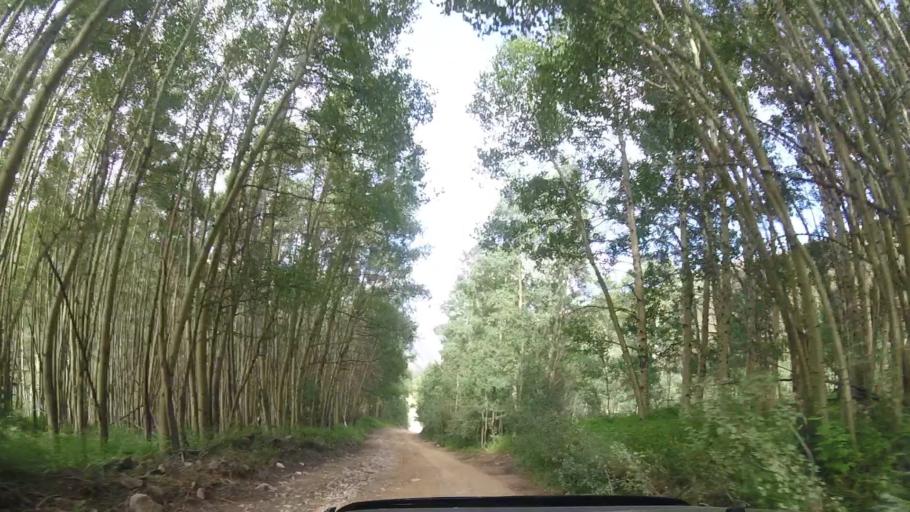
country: US
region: Colorado
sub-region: San Miguel County
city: Telluride
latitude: 37.8596
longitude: -107.7992
